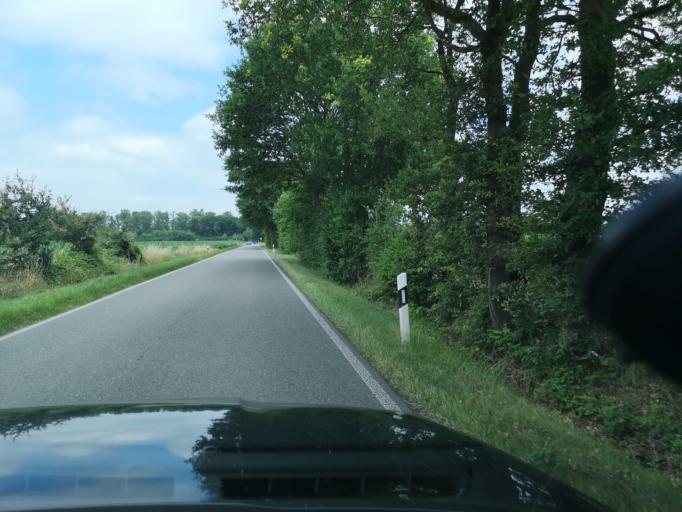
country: DE
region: North Rhine-Westphalia
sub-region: Regierungsbezirk Munster
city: Rhede
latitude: 51.8689
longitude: 6.6898
